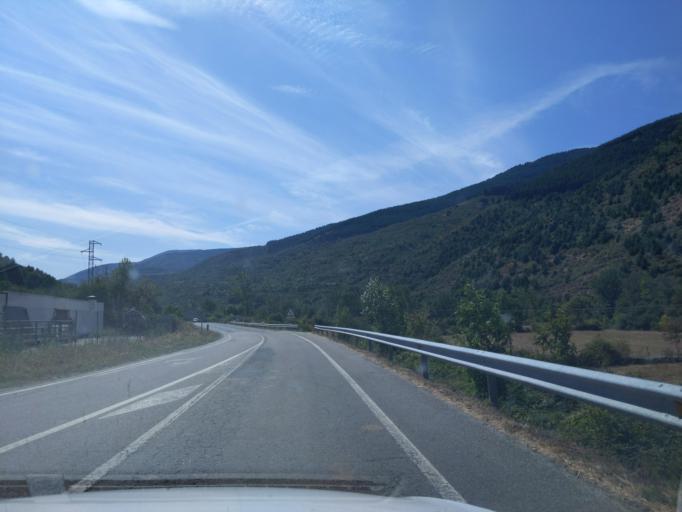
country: ES
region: La Rioja
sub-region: Provincia de La Rioja
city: Ezcaray
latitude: 42.3052
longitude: -3.0217
